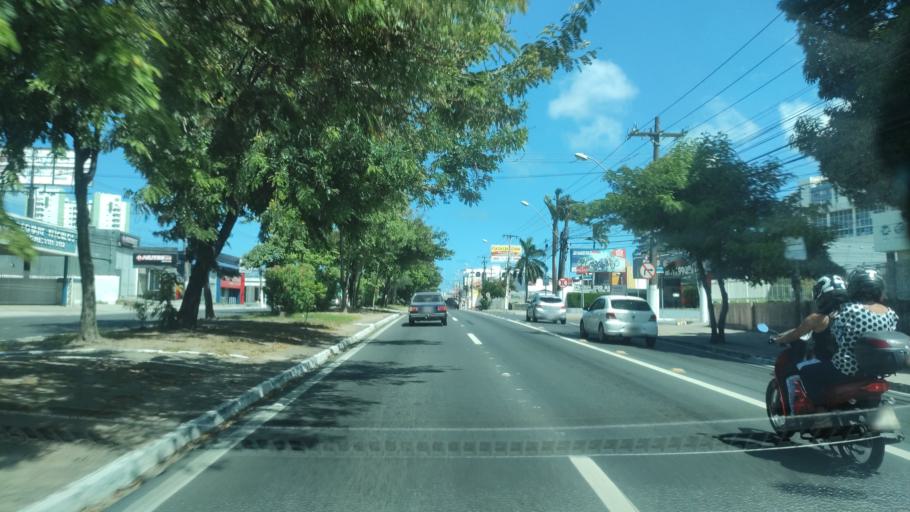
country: BR
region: Alagoas
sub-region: Maceio
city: Maceio
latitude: -9.6407
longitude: -35.7354
